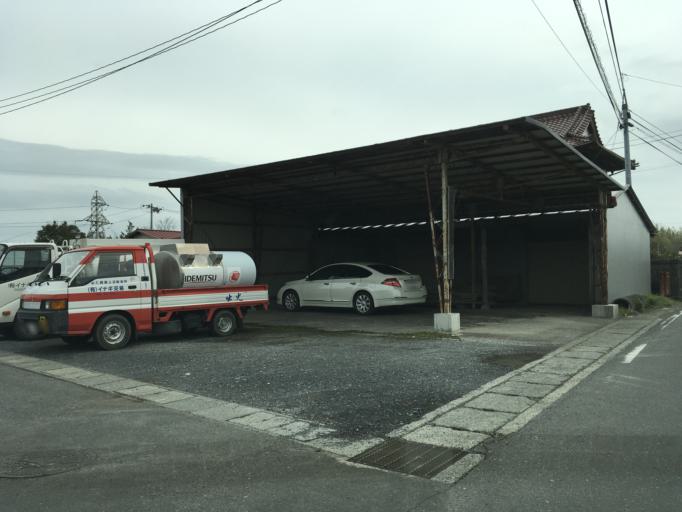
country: JP
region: Iwate
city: Ichinoseki
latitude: 38.7378
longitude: 141.2654
